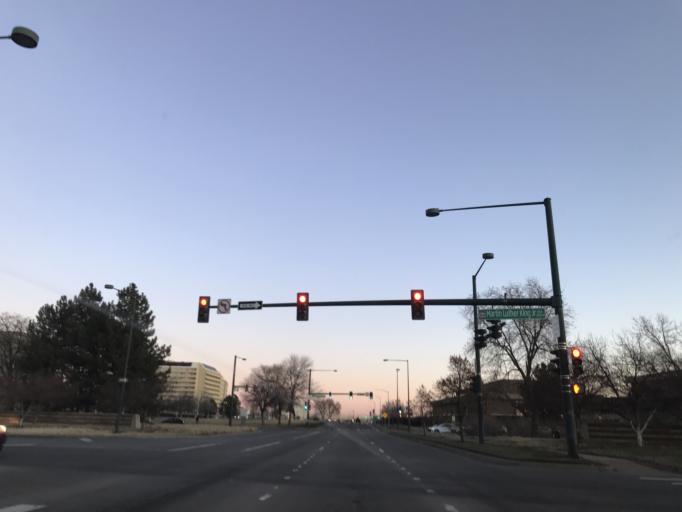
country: US
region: Colorado
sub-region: Adams County
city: Commerce City
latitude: 39.7610
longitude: -104.9028
